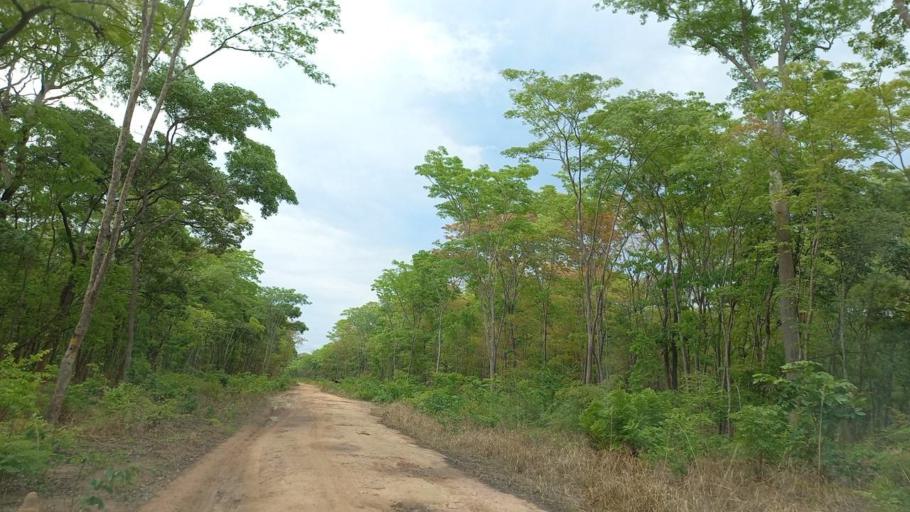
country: ZM
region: North-Western
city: Kalengwa
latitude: -13.5613
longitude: 24.9726
